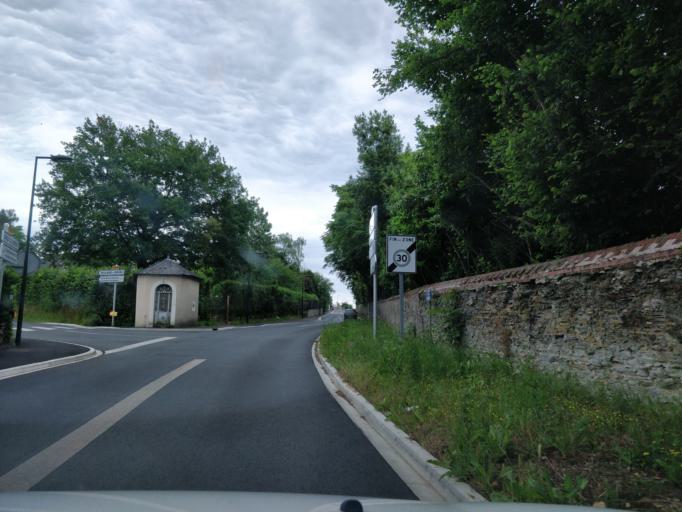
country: FR
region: Pays de la Loire
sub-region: Departement de Maine-et-Loire
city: Feneu
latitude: 47.5695
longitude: -0.5902
